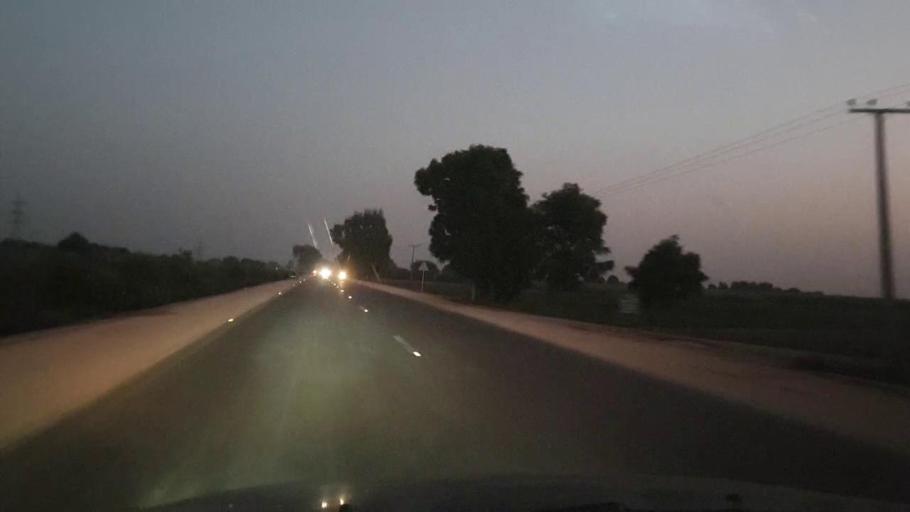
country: PK
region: Sindh
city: Tando Allahyar
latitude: 25.3899
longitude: 68.7697
